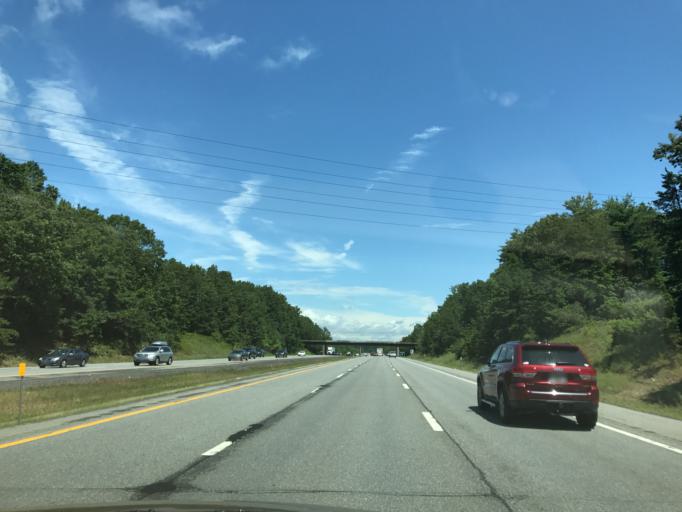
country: US
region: New York
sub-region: Warren County
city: West Glens Falls
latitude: 43.2561
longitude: -73.6804
